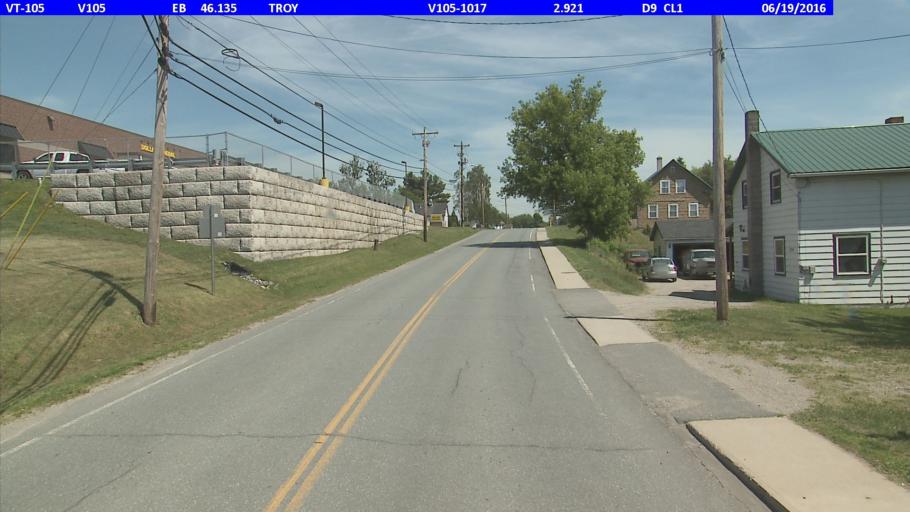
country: US
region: Vermont
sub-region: Orleans County
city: Newport
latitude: 44.9955
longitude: -72.3988
